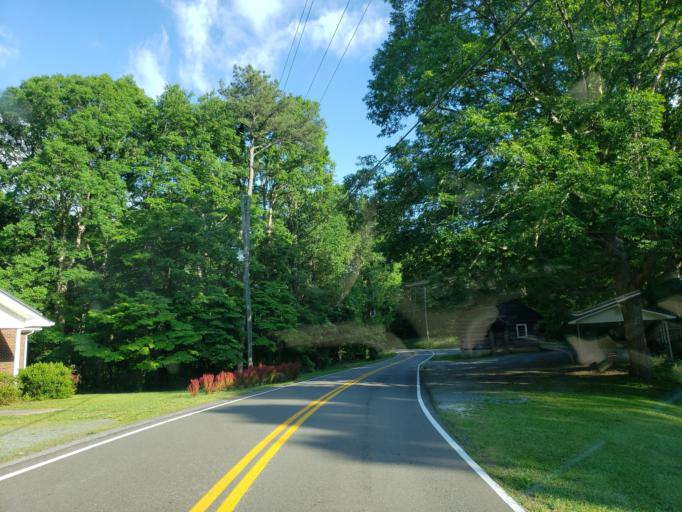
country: US
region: Georgia
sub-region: Murray County
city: Chatsworth
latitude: 34.6618
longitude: -84.6432
